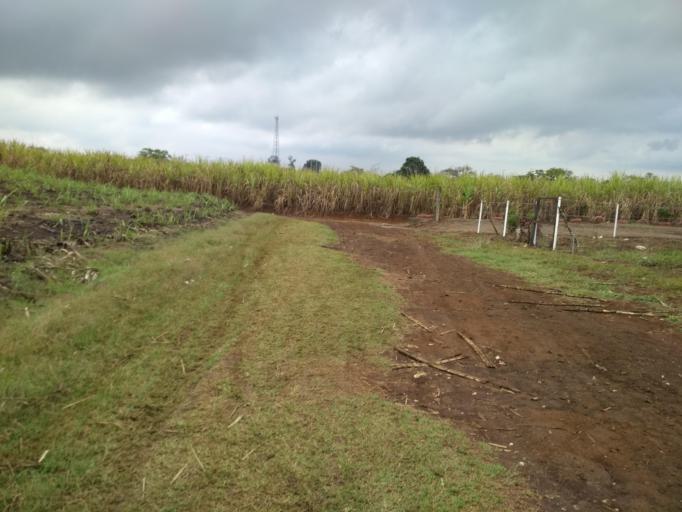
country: MX
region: Veracruz
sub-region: Cordoba
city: San Jose de Tapia
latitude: 18.8506
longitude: -96.9628
